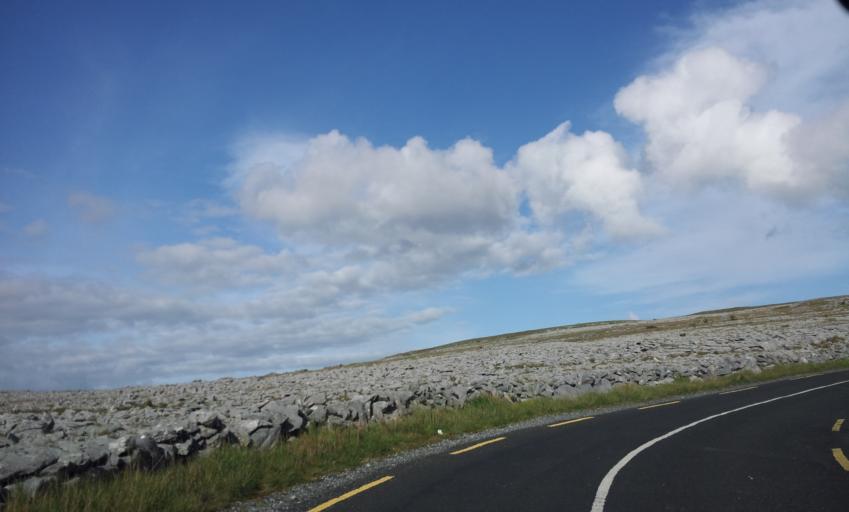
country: IE
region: Connaught
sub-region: County Galway
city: Bearna
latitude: 53.0776
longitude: -9.1594
